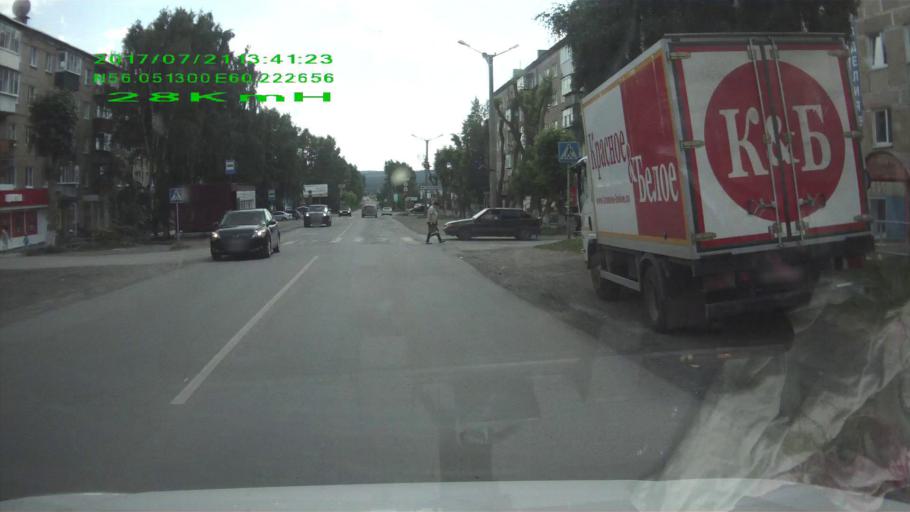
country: RU
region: Chelyabinsk
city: Verkhniy Ufaley
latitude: 56.0510
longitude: 60.2228
